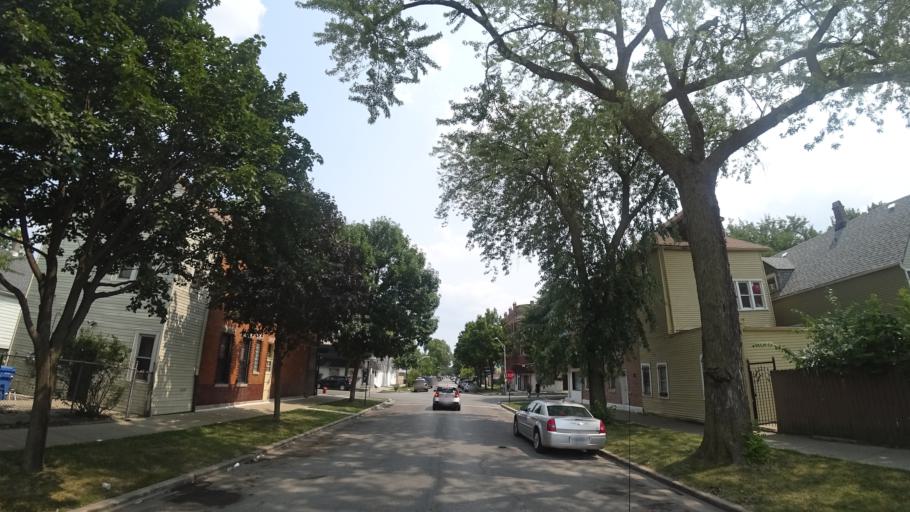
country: US
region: Illinois
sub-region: Cook County
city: Cicero
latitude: 41.8386
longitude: -87.7286
